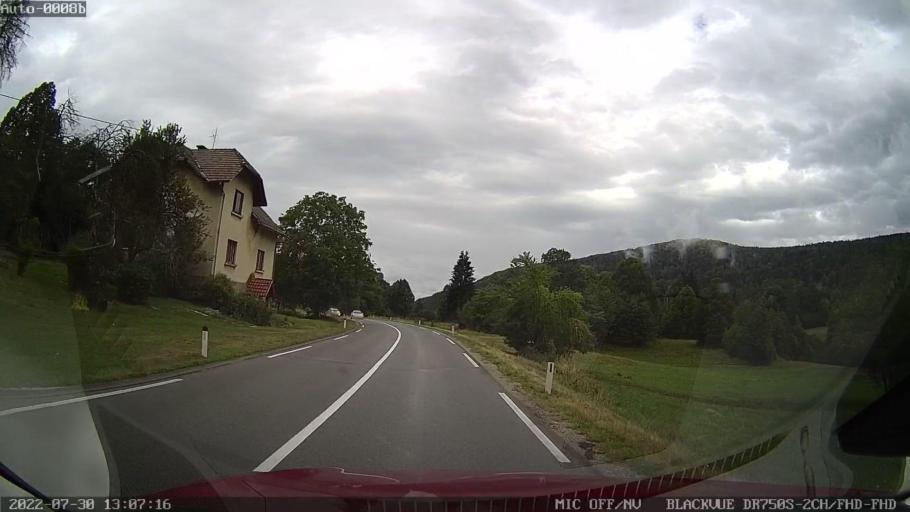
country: SI
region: Semic
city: Semic
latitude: 45.6658
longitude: 15.1080
